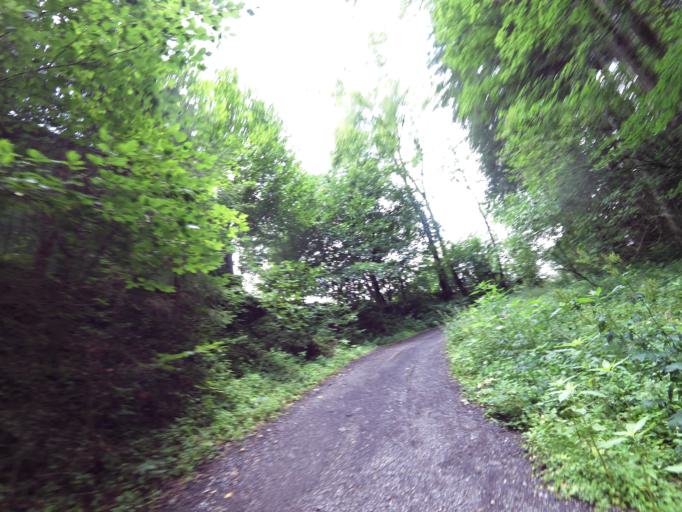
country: DE
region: Bavaria
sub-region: Swabia
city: Weiler-Simmerberg
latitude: 47.6093
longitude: 9.9290
